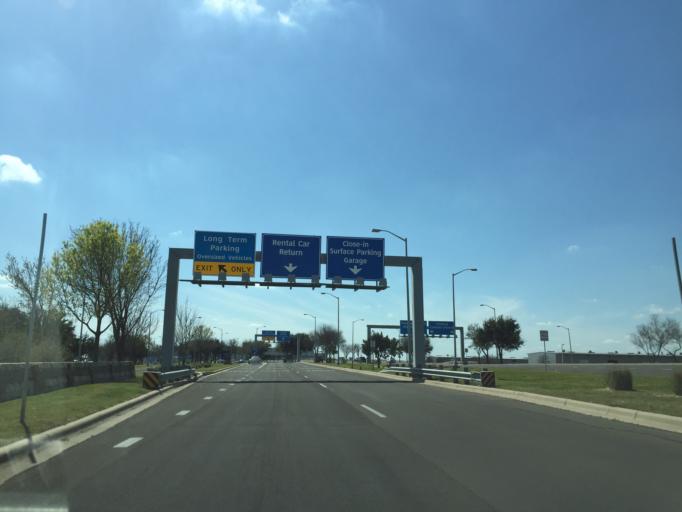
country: US
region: Texas
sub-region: Travis County
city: Austin
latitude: 30.2073
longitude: -97.6709
